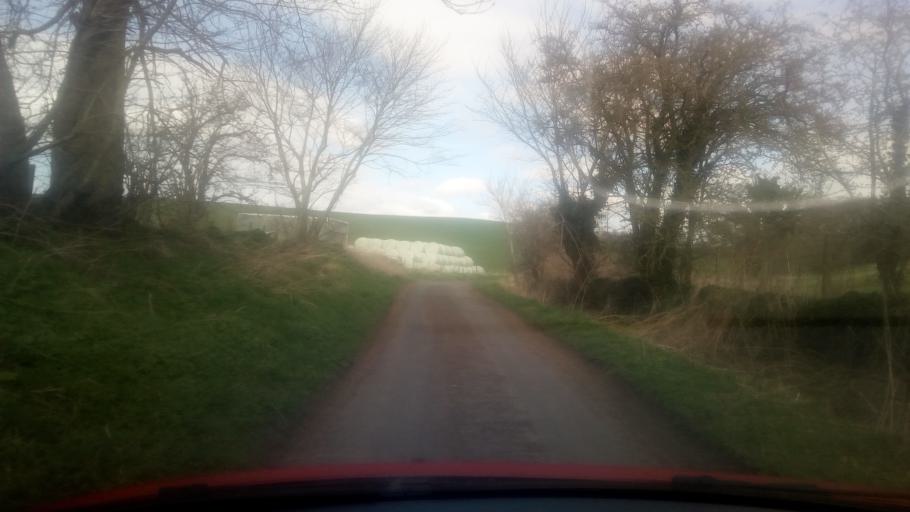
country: GB
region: Scotland
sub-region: The Scottish Borders
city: Jedburgh
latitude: 55.4914
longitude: -2.5392
